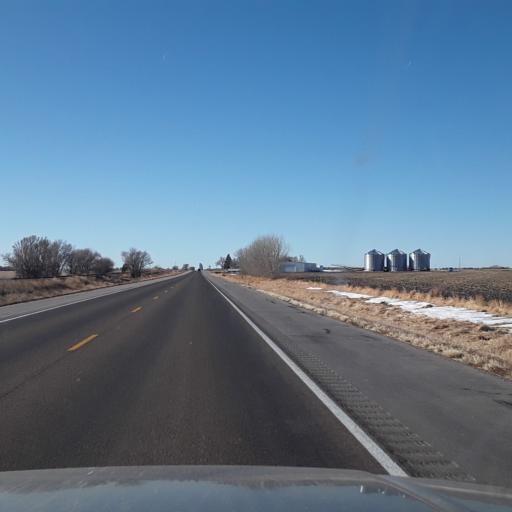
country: US
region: Nebraska
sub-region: Phelps County
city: Holdrege
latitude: 40.4505
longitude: -99.3064
